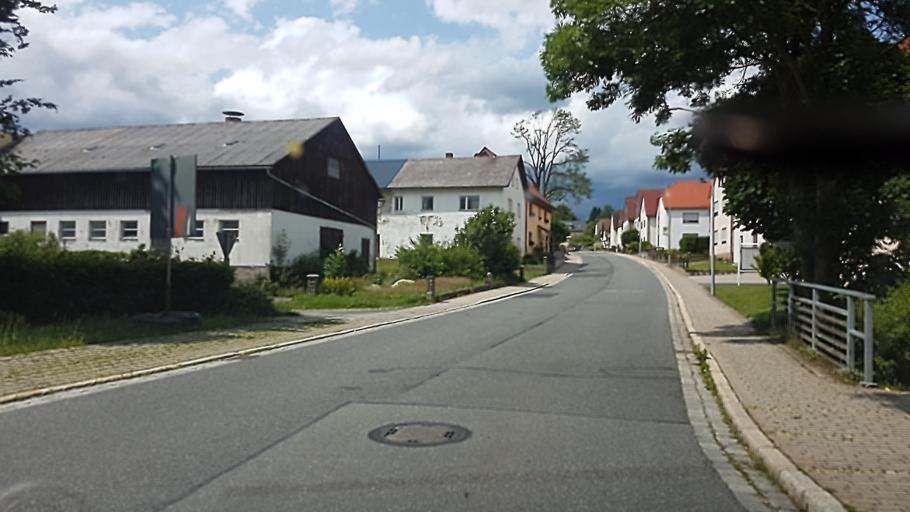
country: DE
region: Bavaria
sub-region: Upper Palatinate
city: Brand
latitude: 49.9588
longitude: 11.9075
